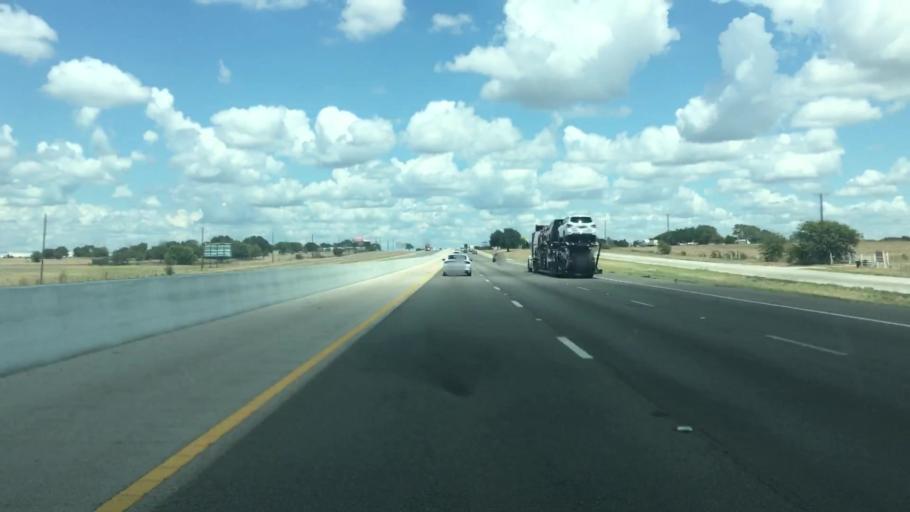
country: US
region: Texas
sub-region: Williamson County
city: Serenada
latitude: 30.7816
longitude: -97.6247
